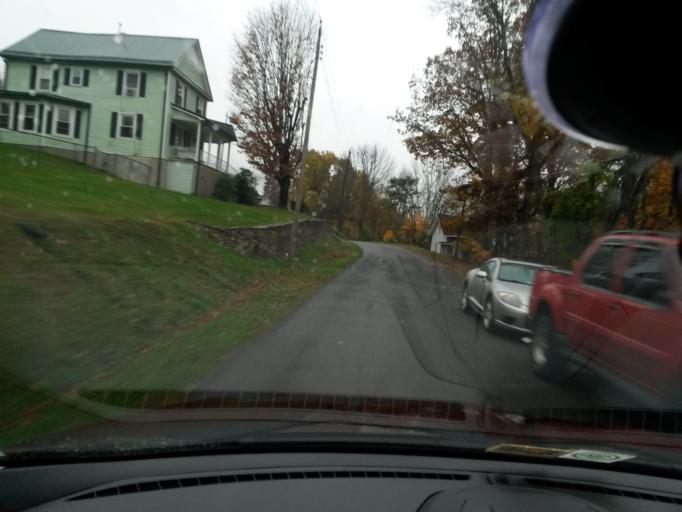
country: US
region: Virginia
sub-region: Alleghany County
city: Clifton Forge
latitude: 37.8205
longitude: -79.8214
